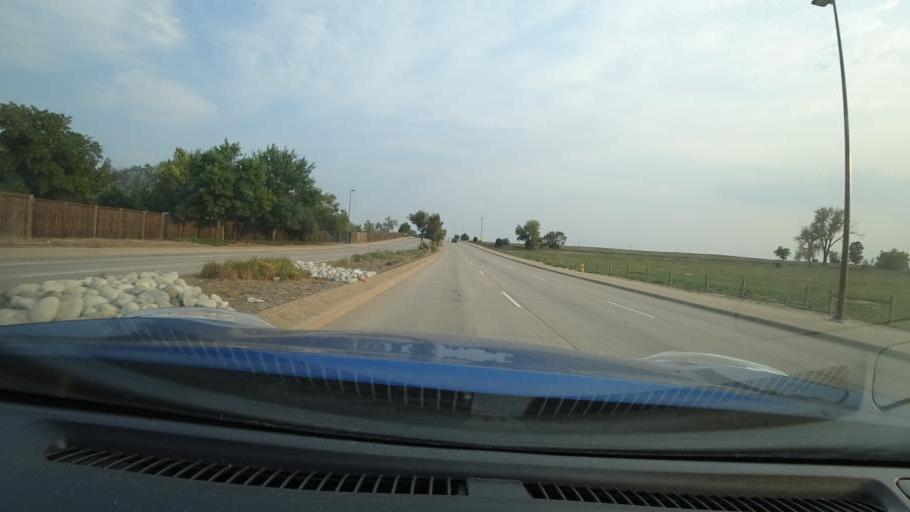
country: US
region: Colorado
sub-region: Adams County
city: Aurora
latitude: 39.7440
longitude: -104.7914
